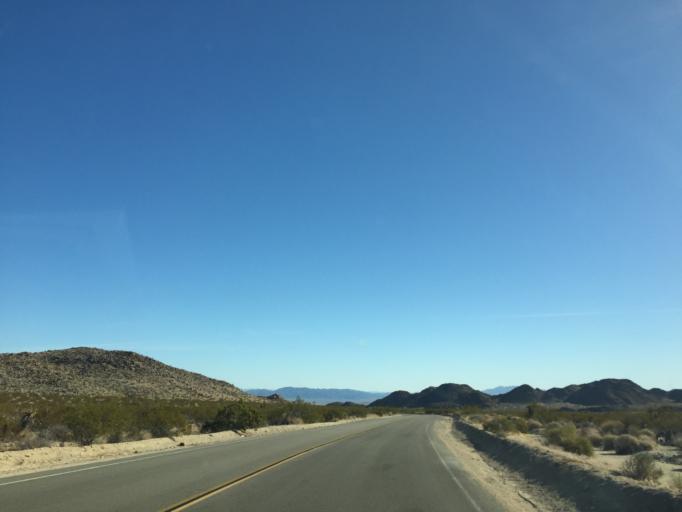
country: US
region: California
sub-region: Riverside County
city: Mecca
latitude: 33.8160
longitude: -115.7671
